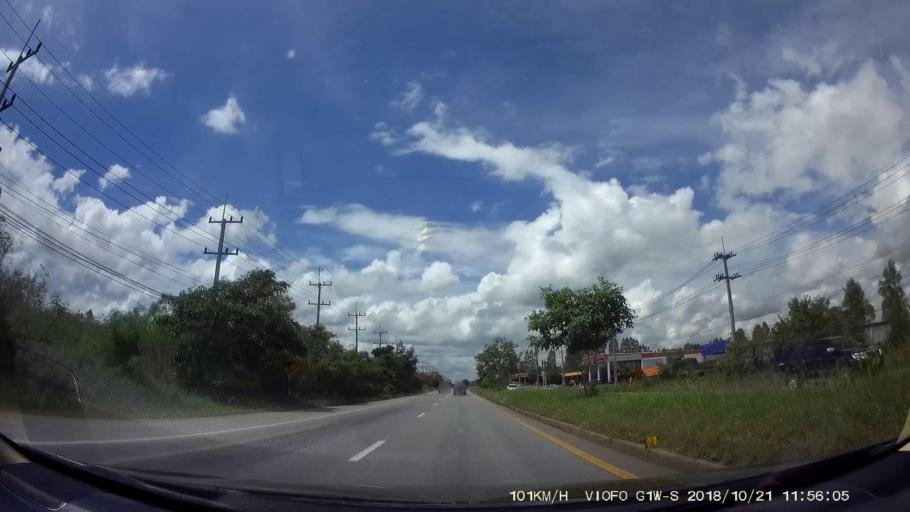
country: TH
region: Chaiyaphum
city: Chatturat
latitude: 15.5779
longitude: 101.8810
